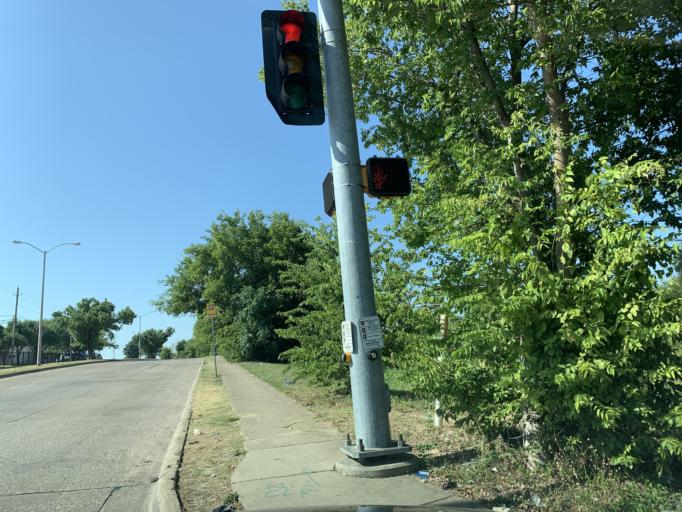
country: US
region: Texas
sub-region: Dallas County
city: Hutchins
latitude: 32.6760
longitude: -96.7640
